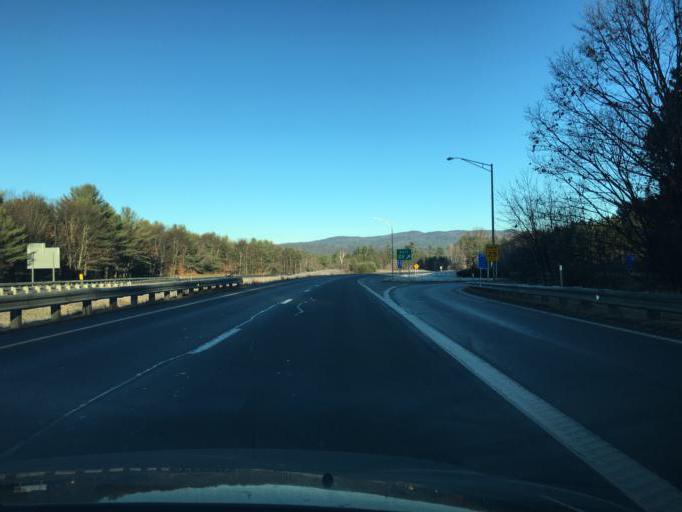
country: US
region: New Hampshire
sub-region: Belknap County
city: Sanbornton
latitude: 43.5050
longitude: -71.6155
